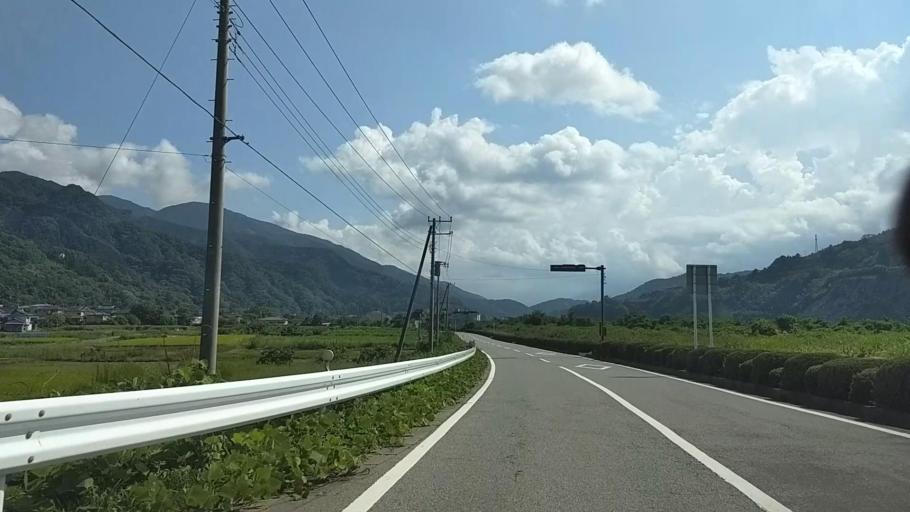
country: JP
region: Shizuoka
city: Fujinomiya
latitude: 35.3940
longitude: 138.4500
